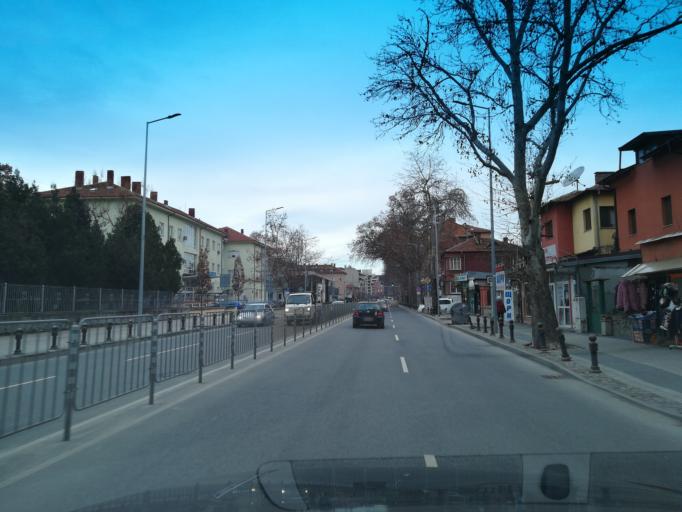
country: BG
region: Plovdiv
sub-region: Obshtina Plovdiv
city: Plovdiv
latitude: 42.1392
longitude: 24.7380
